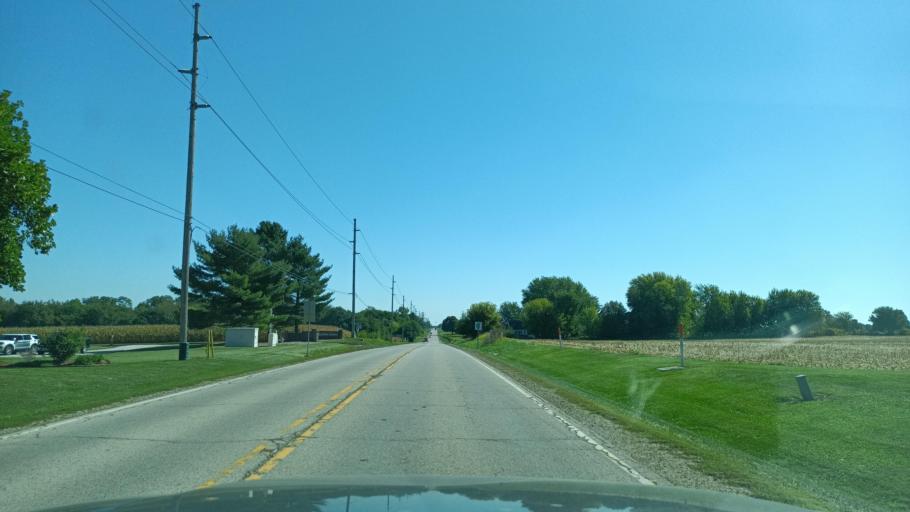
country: US
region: Illinois
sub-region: Peoria County
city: Dunlap
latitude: 40.7840
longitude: -89.7152
